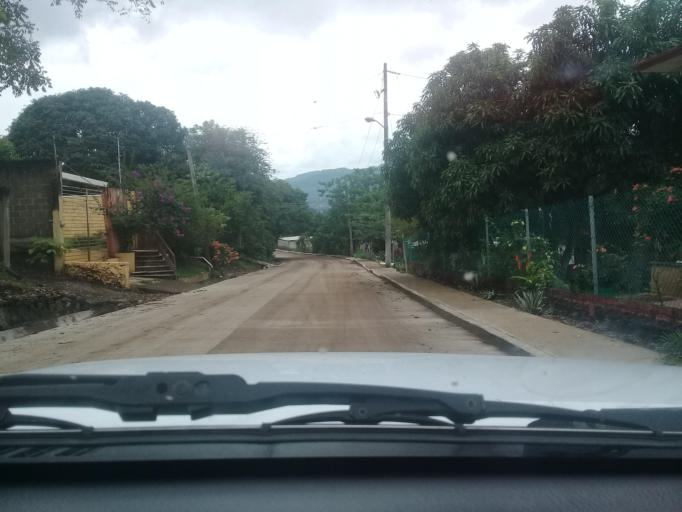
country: MX
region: Veracruz
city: Comoapan
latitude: 18.4142
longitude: -95.1822
